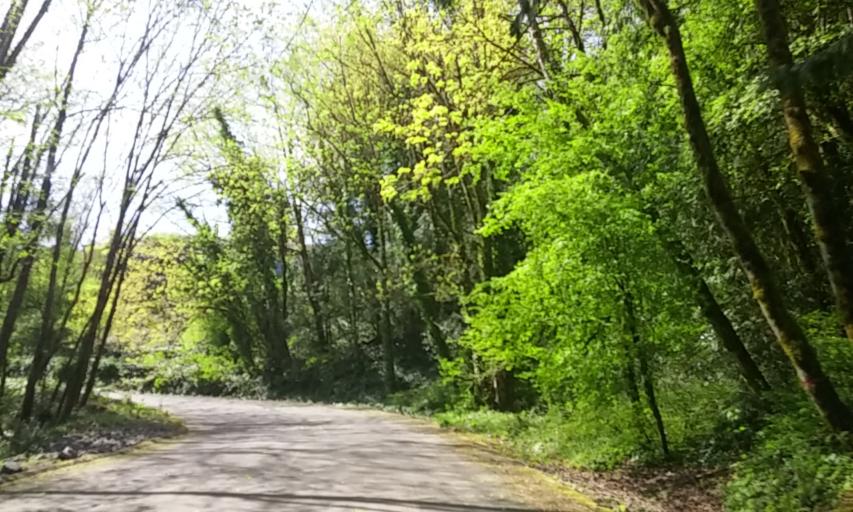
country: US
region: Oregon
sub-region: Washington County
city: West Haven-Sylvan
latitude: 45.5244
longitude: -122.7437
